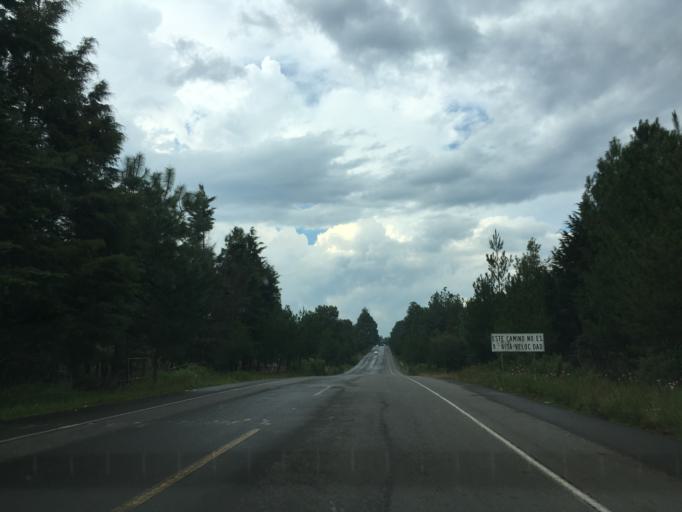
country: MX
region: Michoacan
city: Angahuan
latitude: 19.5420
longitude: -102.2055
